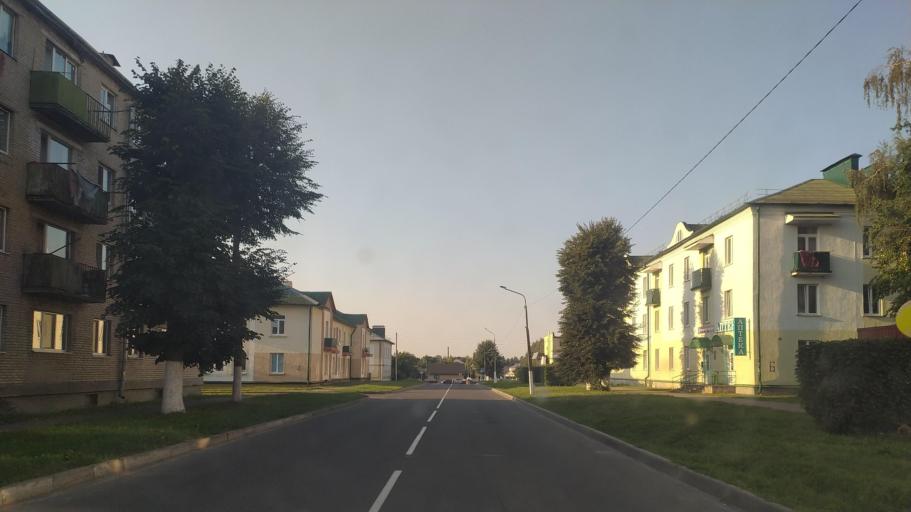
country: BY
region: Brest
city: Byaroza
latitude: 52.5408
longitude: 24.9841
